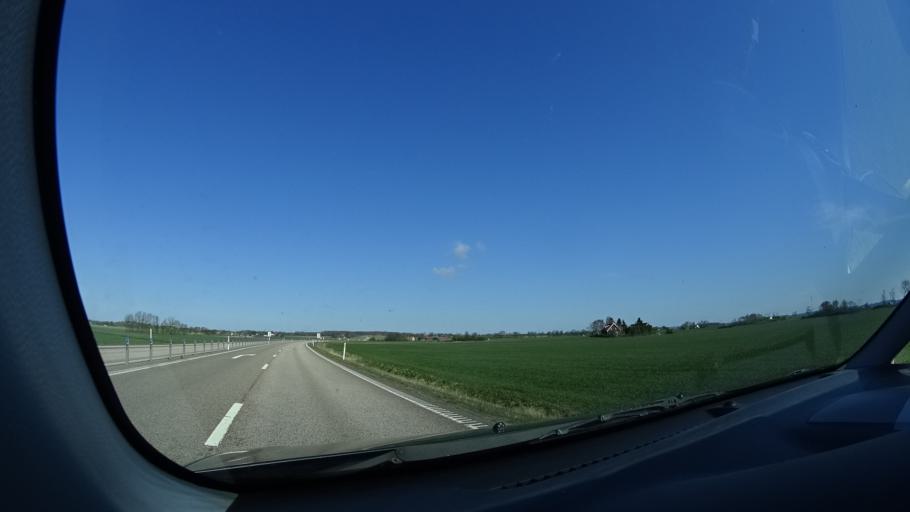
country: SE
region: Skane
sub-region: Astorps Kommun
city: Astorp
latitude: 56.1533
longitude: 12.9219
